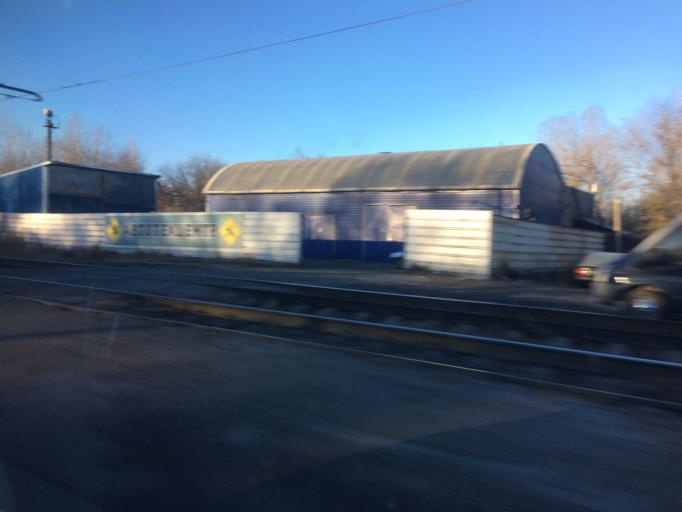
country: RU
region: Chelyabinsk
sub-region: Gorod Magnitogorsk
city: Magnitogorsk
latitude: 53.4052
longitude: 59.0284
